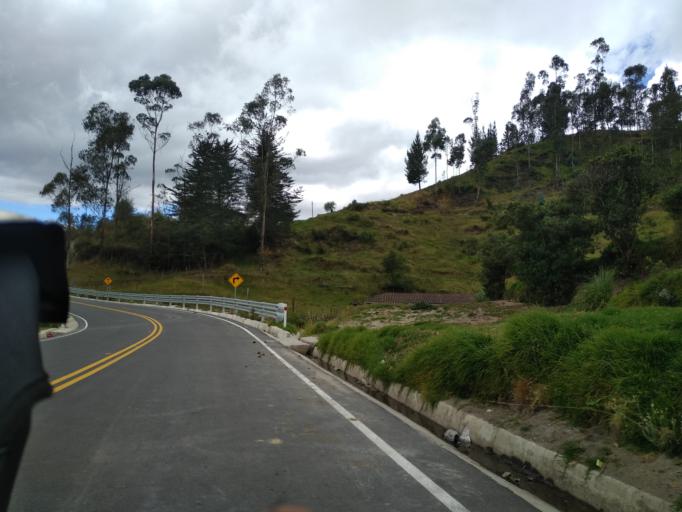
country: EC
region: Cotopaxi
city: Saquisili
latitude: -0.7747
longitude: -78.9093
